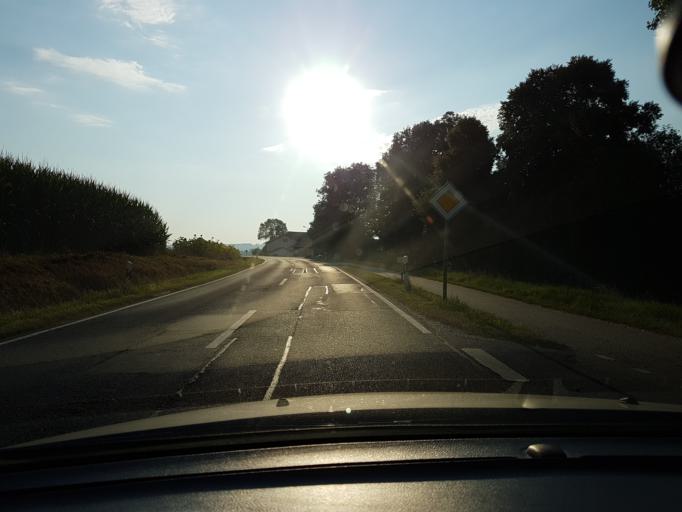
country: DE
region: Bavaria
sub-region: Lower Bavaria
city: Schalkham
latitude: 48.4998
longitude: 12.4166
